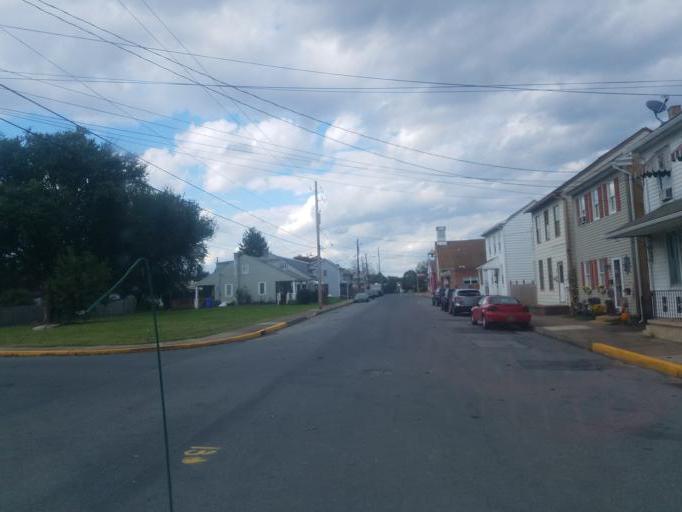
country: US
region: Pennsylvania
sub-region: Dauphin County
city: Middletown
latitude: 40.1875
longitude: -76.7343
